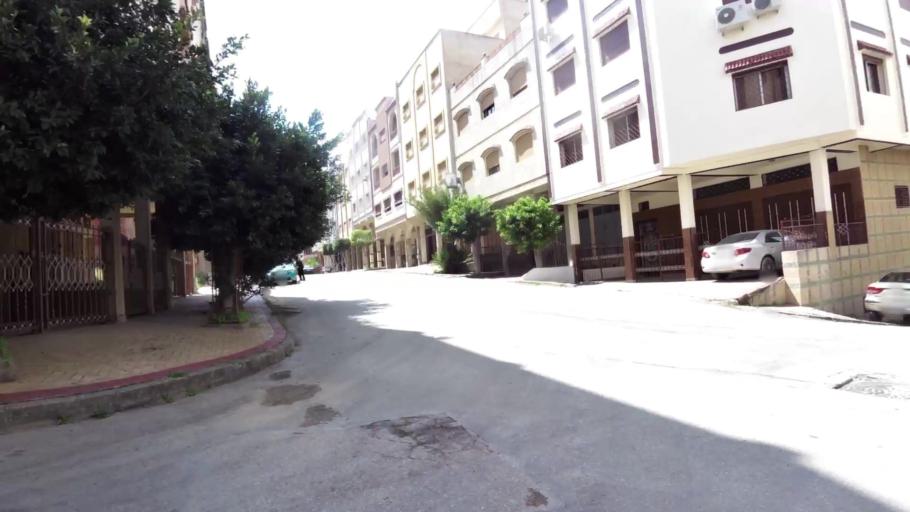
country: MA
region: Tanger-Tetouan
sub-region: Tanger-Assilah
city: Tangier
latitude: 35.7530
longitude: -5.8309
